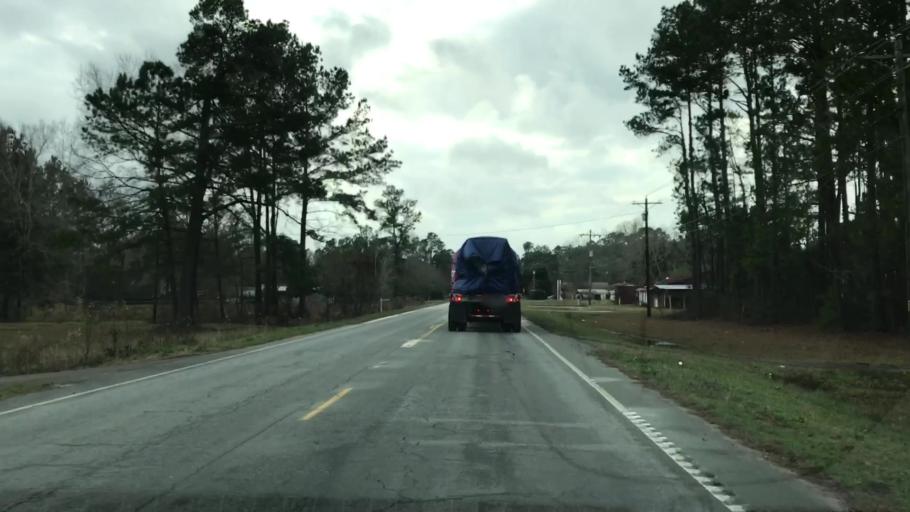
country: US
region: South Carolina
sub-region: Berkeley County
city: Bonneau Beach
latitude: 33.2768
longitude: -79.8892
